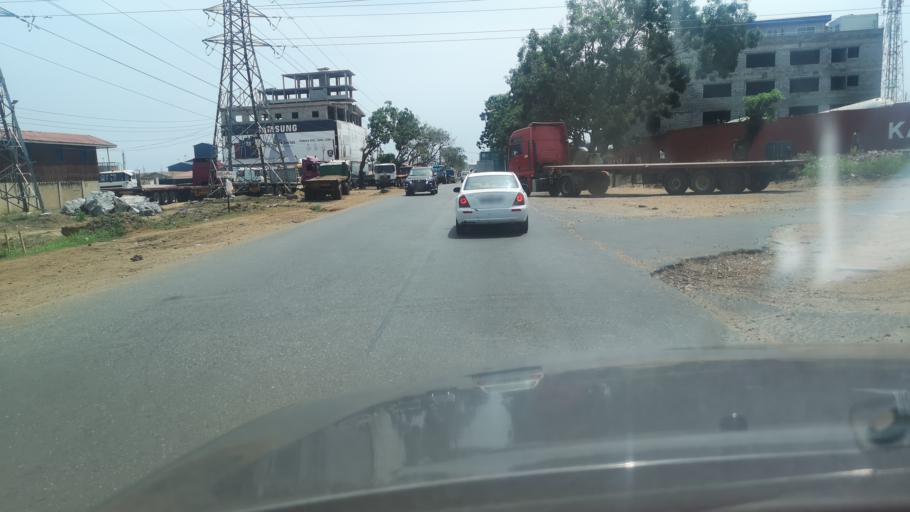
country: GH
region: Greater Accra
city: Tema
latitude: 5.6324
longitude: -0.0041
